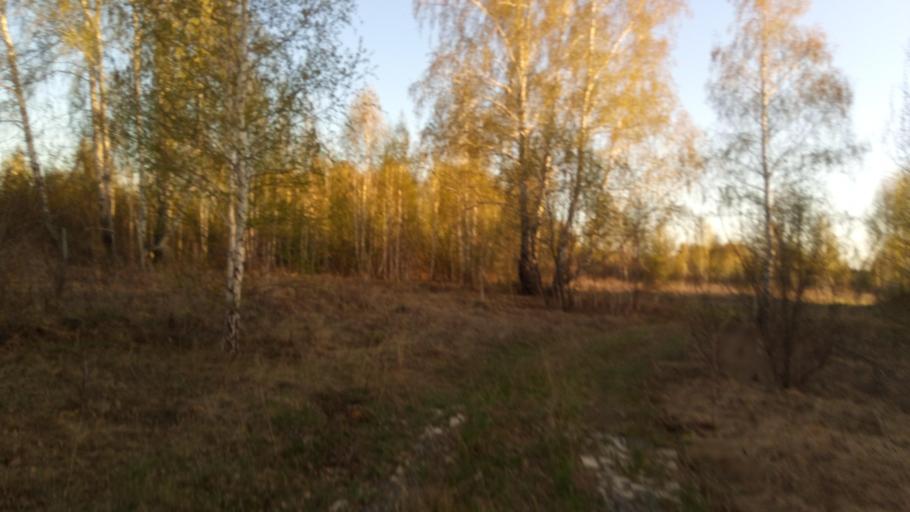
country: RU
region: Chelyabinsk
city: Timiryazevskiy
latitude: 54.9938
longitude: 60.8553
